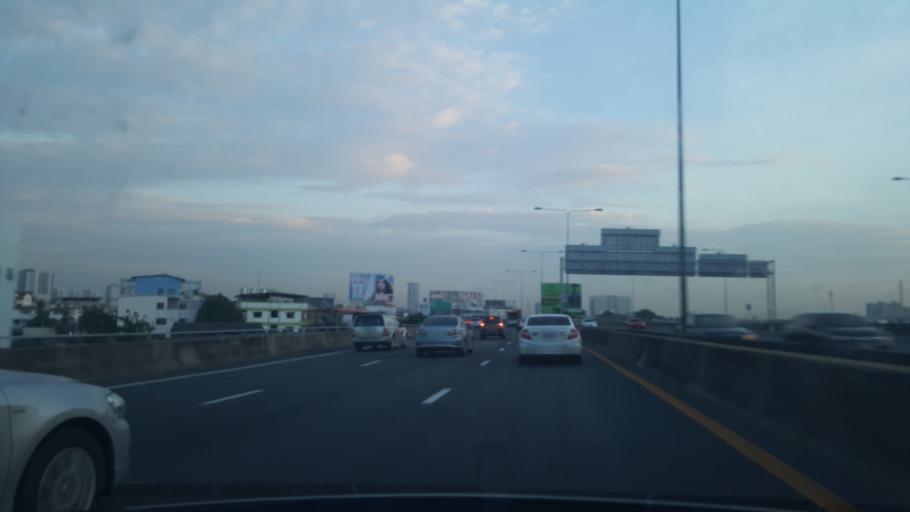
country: TH
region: Bangkok
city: Sathon
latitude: 13.7016
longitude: 100.5191
